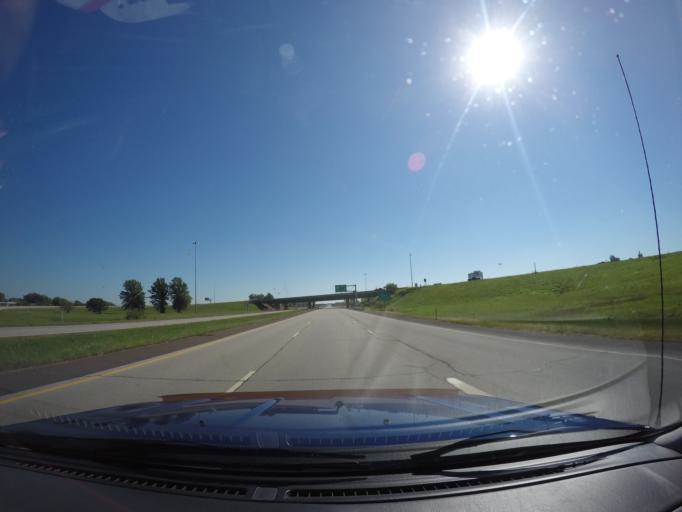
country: US
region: Kansas
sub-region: Shawnee County
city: Topeka
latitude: 39.0905
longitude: -95.7297
